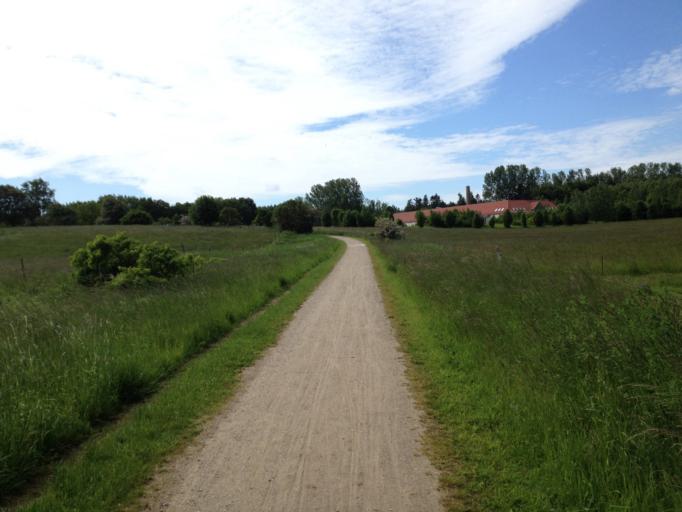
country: DK
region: Capital Region
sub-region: Fredensborg Kommune
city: Niva
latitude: 55.9281
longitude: 12.4905
